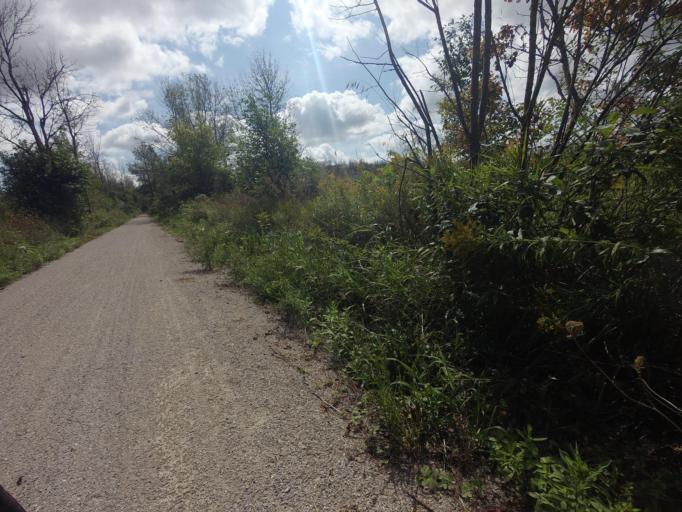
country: CA
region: Ontario
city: Huron East
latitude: 43.6197
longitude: -81.1528
